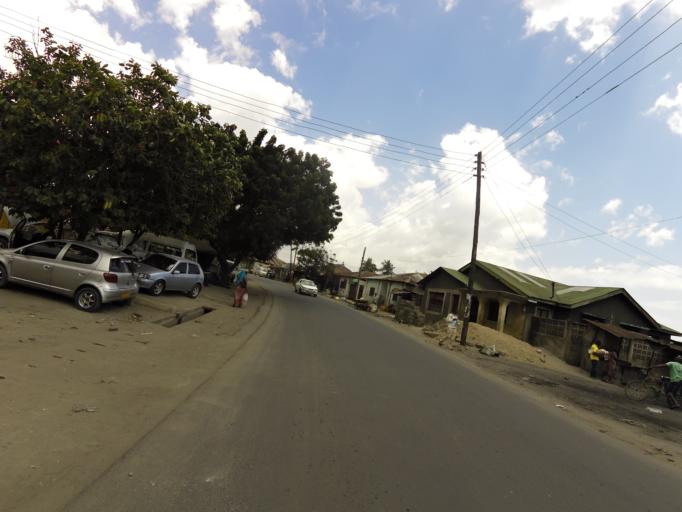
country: TZ
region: Dar es Salaam
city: Magomeni
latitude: -6.8005
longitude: 39.2541
